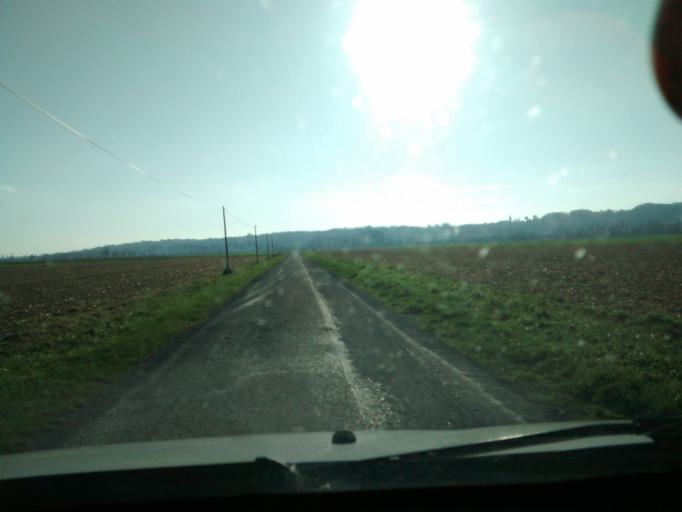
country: FR
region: Brittany
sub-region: Departement d'Ille-et-Vilaine
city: Roz-sur-Couesnon
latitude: 48.6068
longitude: -1.5820
